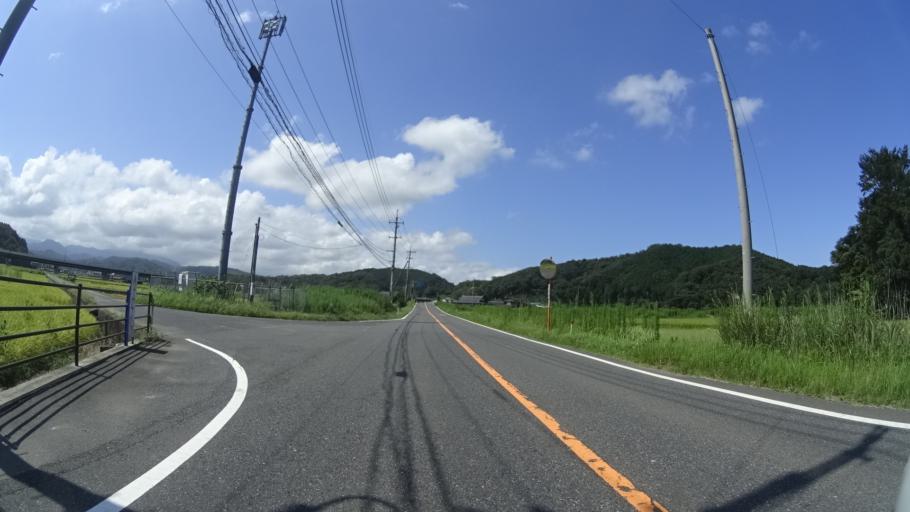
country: JP
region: Tottori
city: Tottori
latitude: 35.4965
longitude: 134.1328
